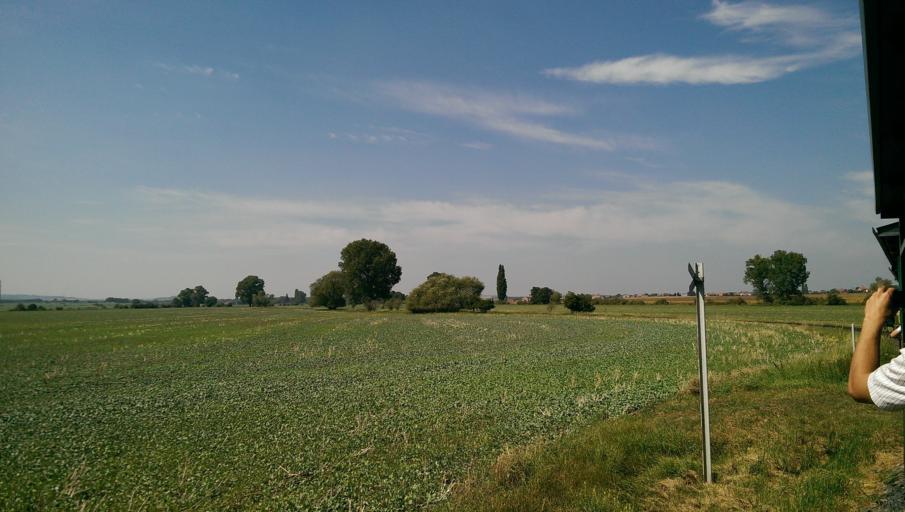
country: CZ
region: Central Bohemia
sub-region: Okres Kolin
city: Kolin
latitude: 50.0531
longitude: 15.2524
